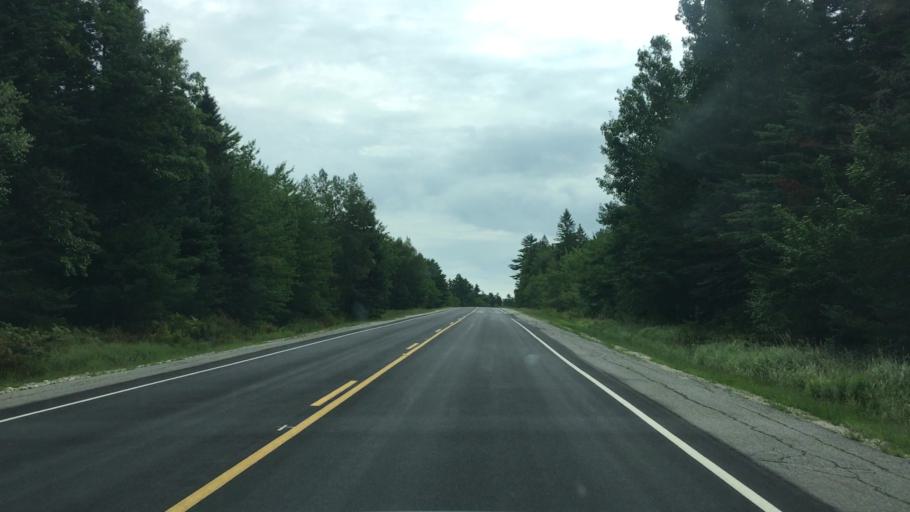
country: US
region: Maine
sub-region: Washington County
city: Addison
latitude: 44.9074
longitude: -67.8349
